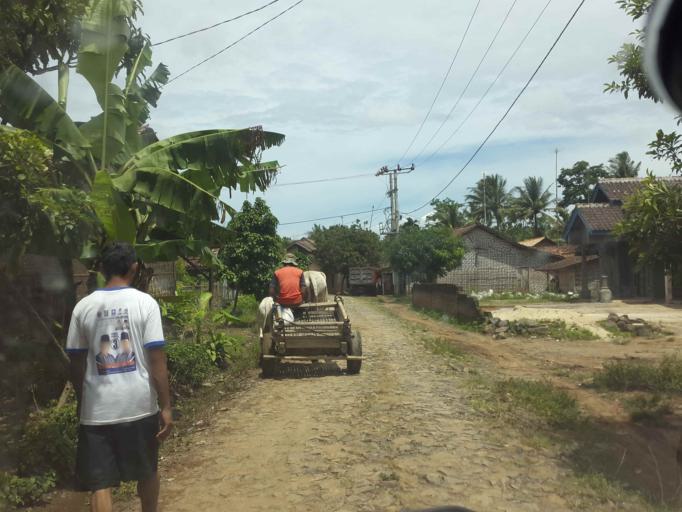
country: ID
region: Lampung
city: Sidorejo
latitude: -5.5594
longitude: 105.4478
